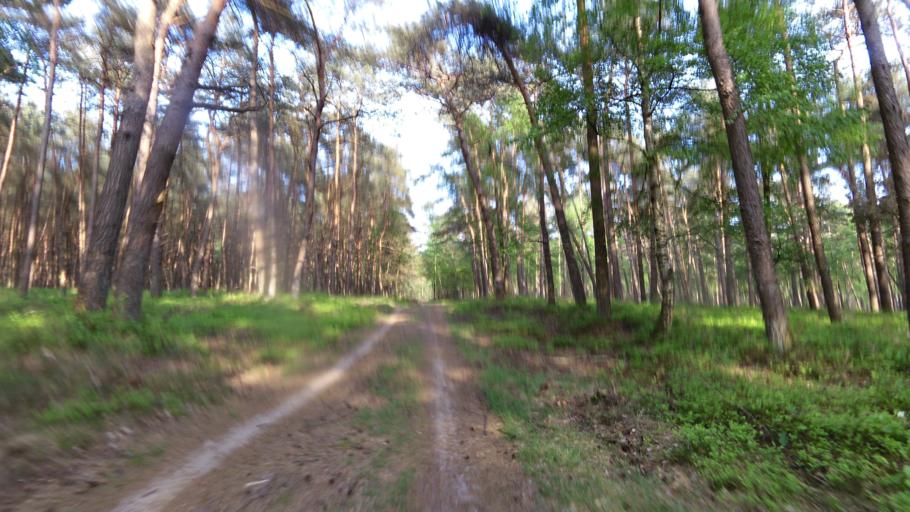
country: NL
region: Gelderland
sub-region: Gemeente Ede
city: Otterlo
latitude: 52.0542
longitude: 5.7461
